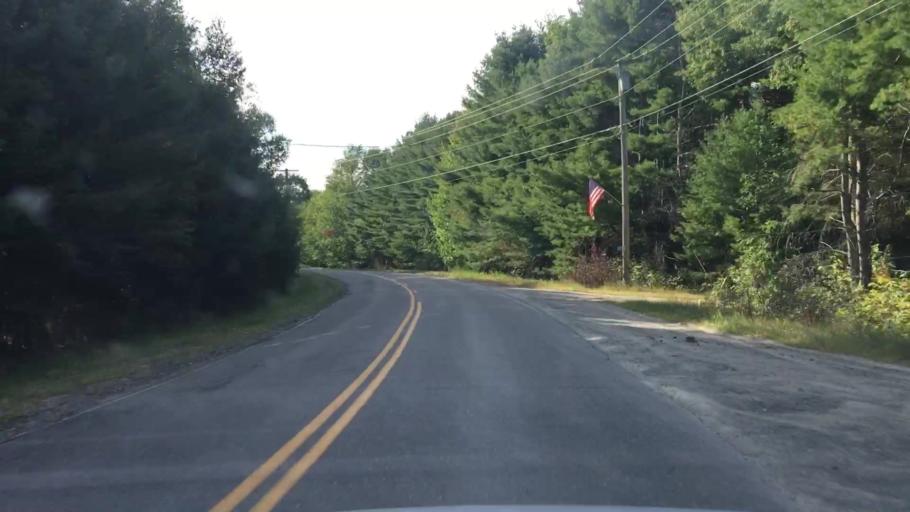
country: US
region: Maine
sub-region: Penobscot County
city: Enfield
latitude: 45.2367
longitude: -68.5456
